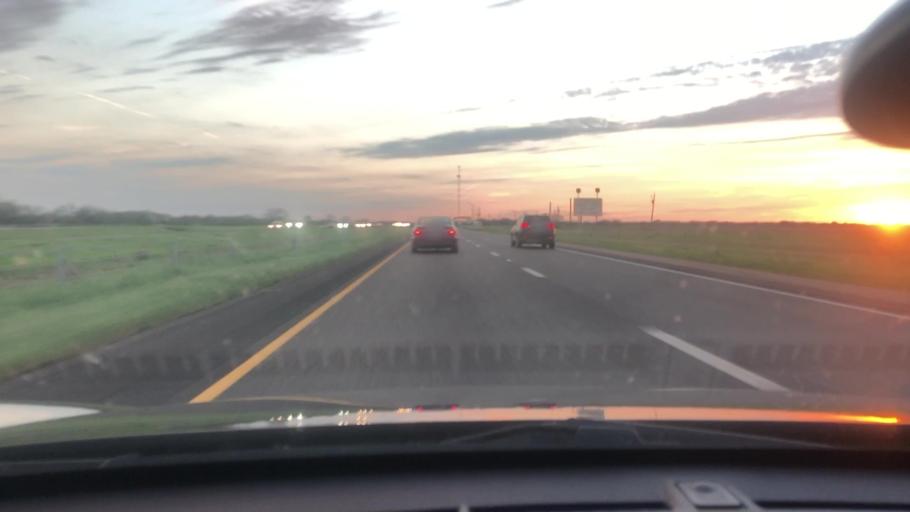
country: US
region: Texas
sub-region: Victoria County
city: Inez
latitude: 28.9303
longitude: -96.7422
